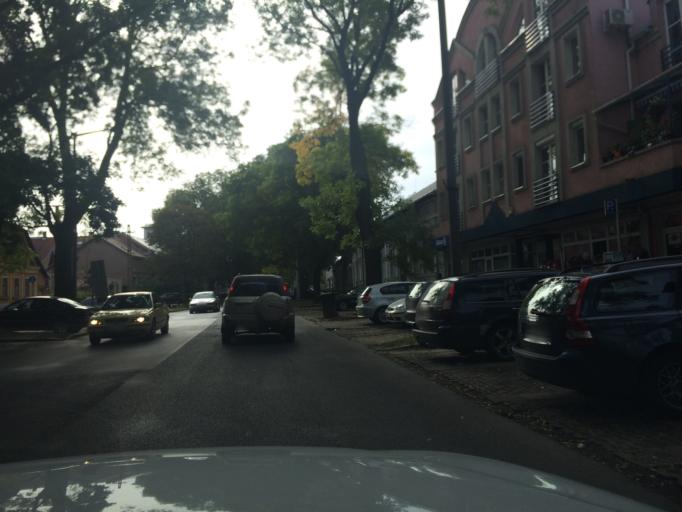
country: HU
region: Szabolcs-Szatmar-Bereg
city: Nyiregyhaza
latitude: 47.9517
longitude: 21.7157
